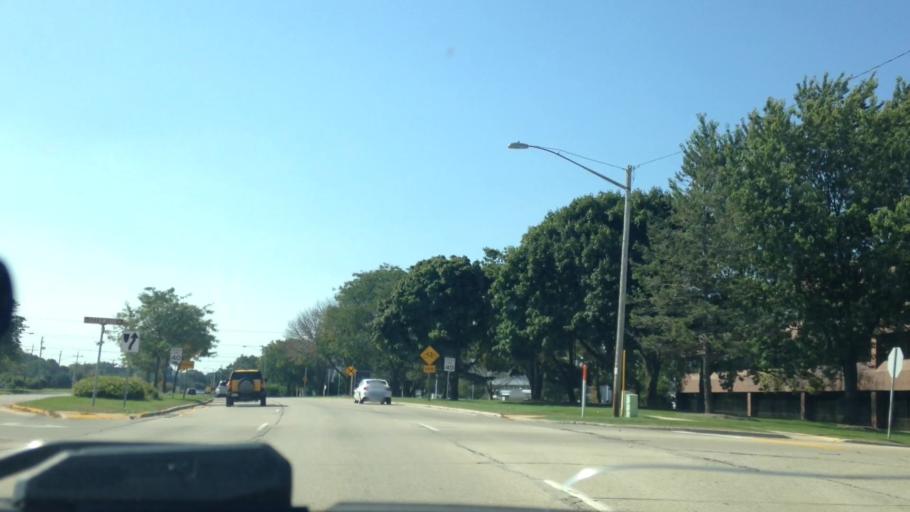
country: US
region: Wisconsin
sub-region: Milwaukee County
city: Brown Deer
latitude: 43.1785
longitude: -87.9640
